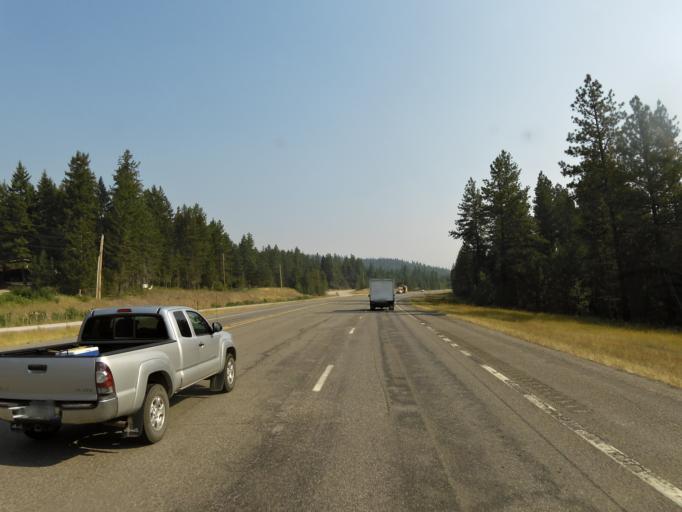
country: US
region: Montana
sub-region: Missoula County
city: Frenchtown
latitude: 47.0642
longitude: -114.0737
